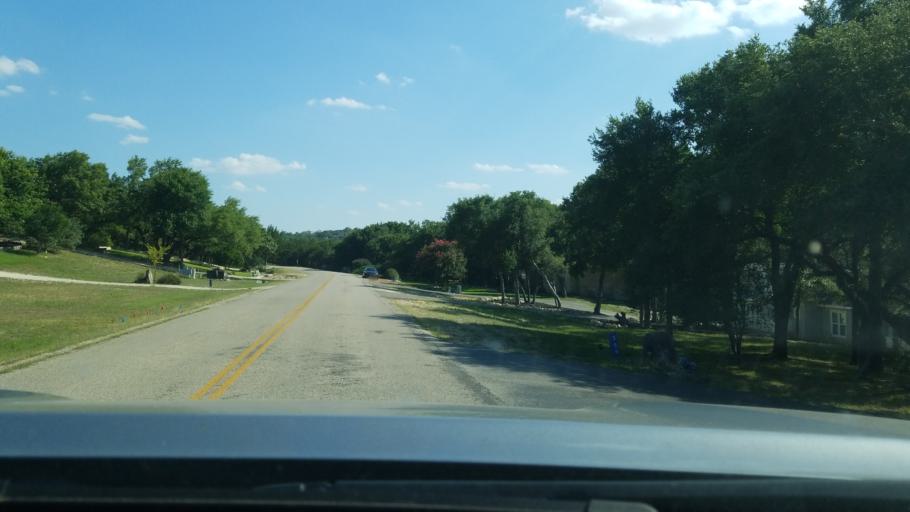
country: US
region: Texas
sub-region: Comal County
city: Bulverde
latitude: 29.8214
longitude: -98.3997
